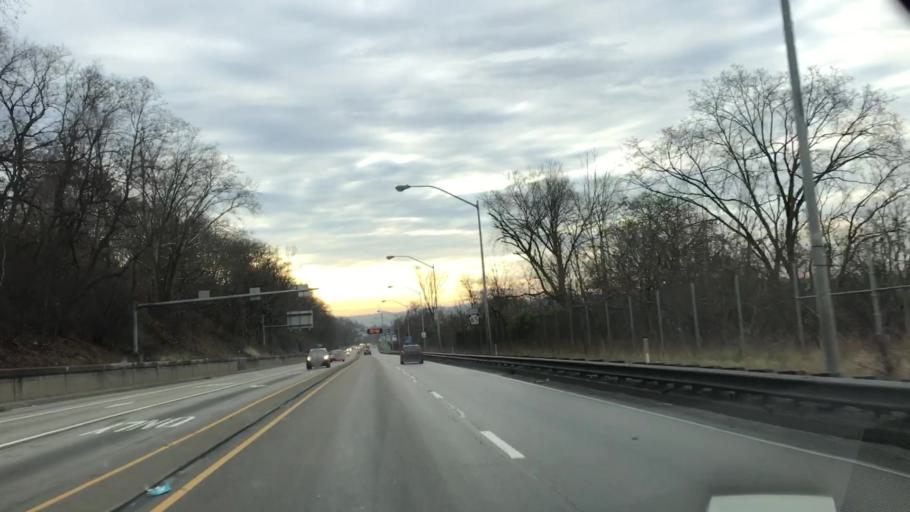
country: US
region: Pennsylvania
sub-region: Allegheny County
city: Bellevue
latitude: 40.4783
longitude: -80.0426
